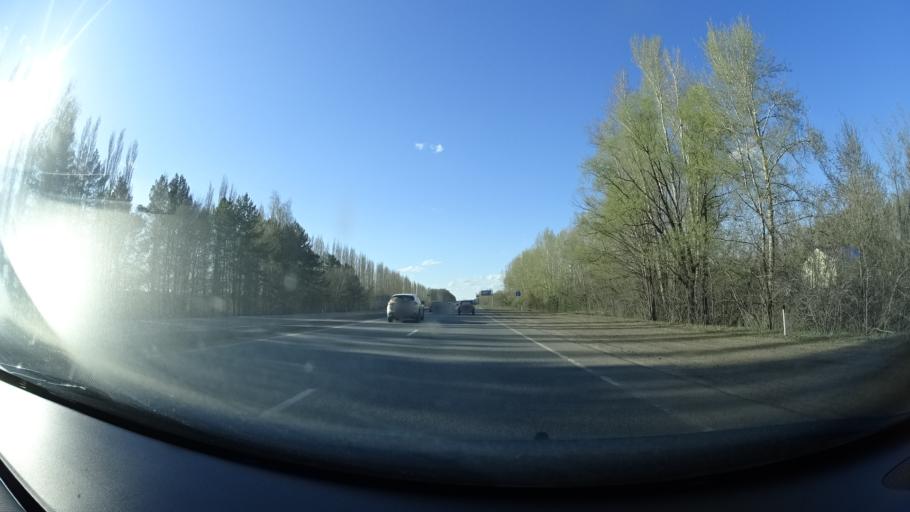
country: RU
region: Bashkortostan
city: Ufa
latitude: 54.5641
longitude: 55.9207
